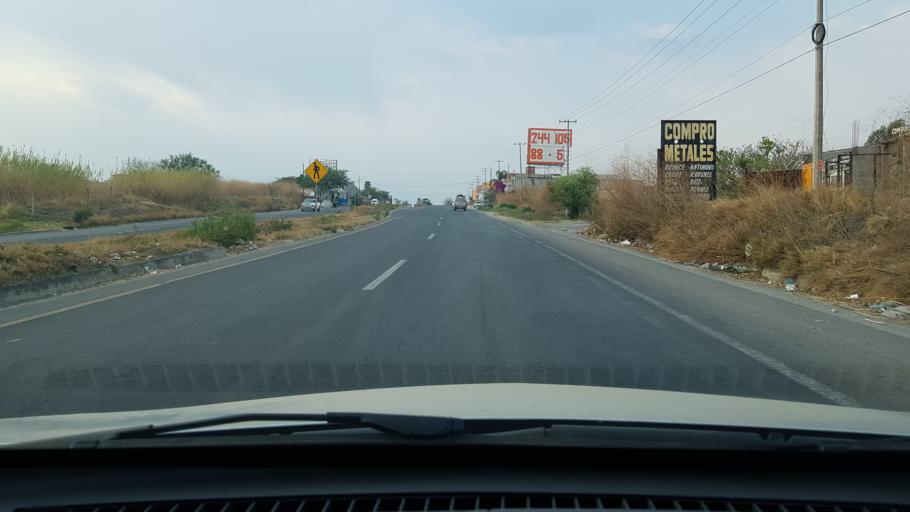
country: MX
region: Morelos
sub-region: Yecapixtla
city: Juan Morales
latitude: 18.8083
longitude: -98.9154
